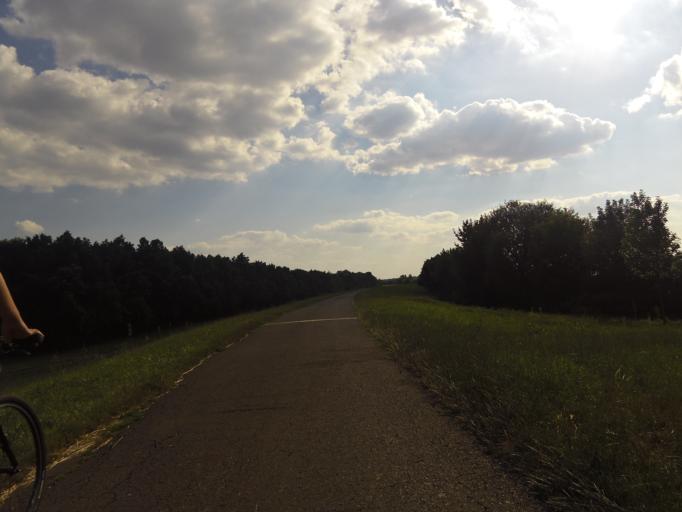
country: HU
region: Jasz-Nagykun-Szolnok
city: Abadszalok
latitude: 47.5252
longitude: 20.6043
